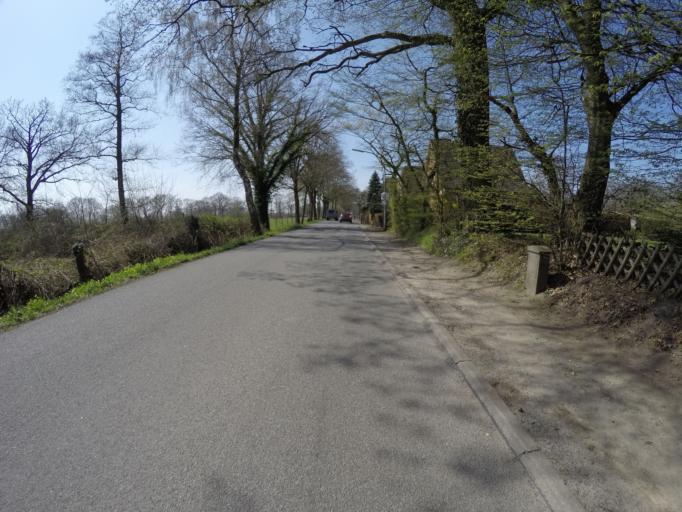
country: DE
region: Schleswig-Holstein
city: Quickborn
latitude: 53.7140
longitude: 9.9124
